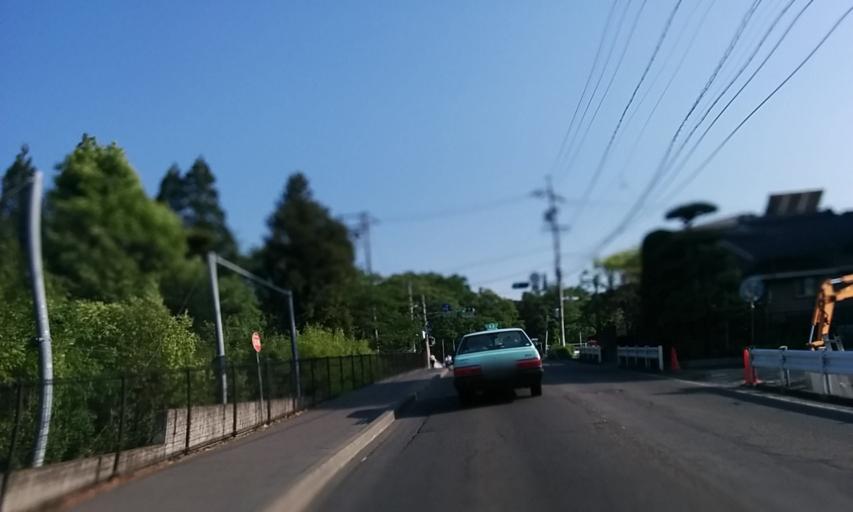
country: JP
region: Nagano
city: Matsumoto
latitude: 36.2280
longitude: 137.9820
